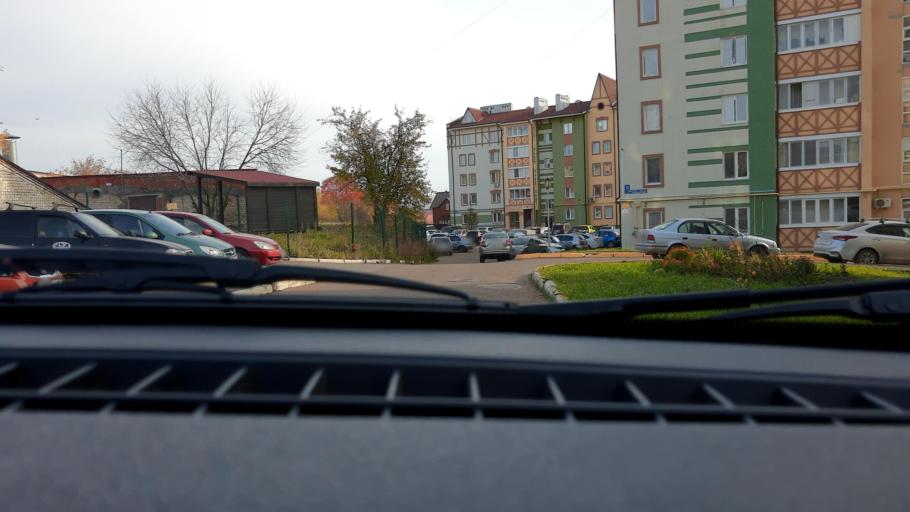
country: RU
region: Bashkortostan
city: Mikhaylovka
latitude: 54.8126
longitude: 55.8946
